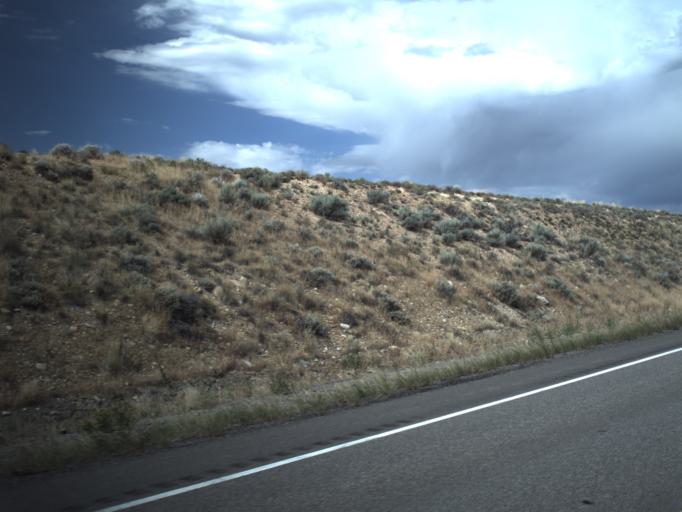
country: US
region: Utah
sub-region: Carbon County
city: East Carbon City
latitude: 39.5172
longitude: -110.5534
